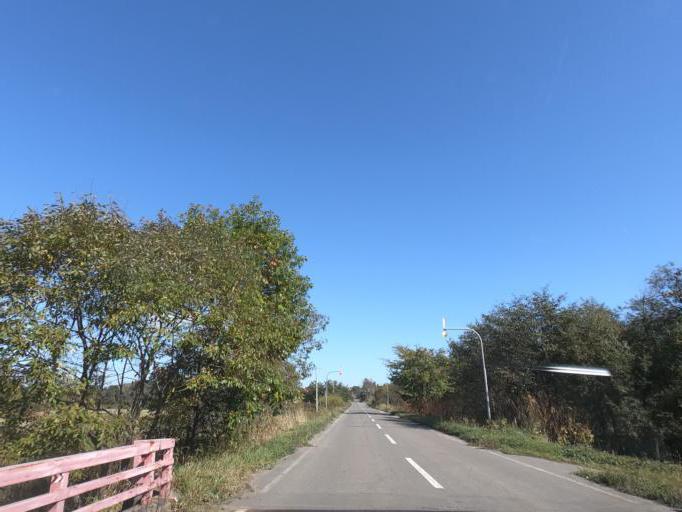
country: JP
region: Hokkaido
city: Obihiro
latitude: 42.6763
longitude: 143.3136
